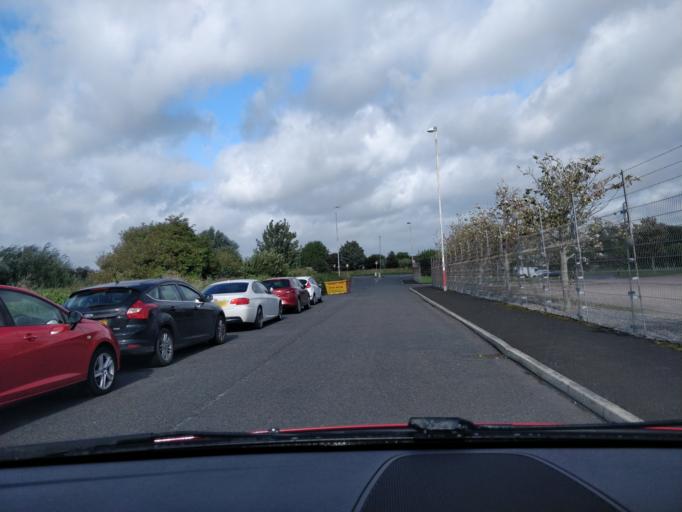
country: GB
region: England
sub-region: Lancashire
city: Banks
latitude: 53.6783
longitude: -2.9532
